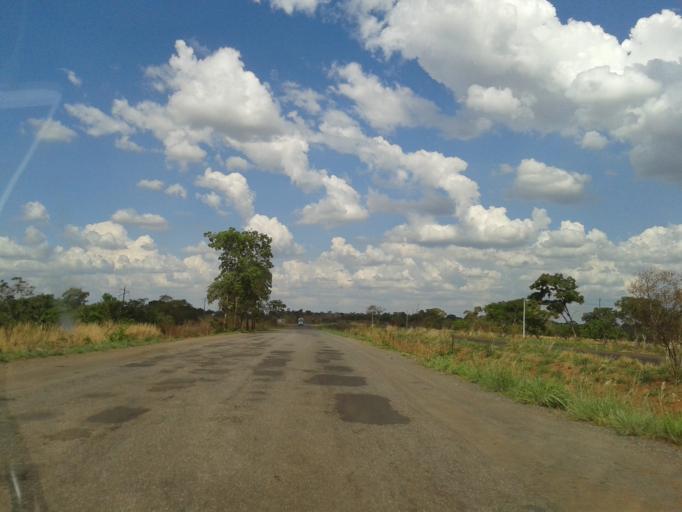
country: BR
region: Goias
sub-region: Caldas Novas
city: Caldas Novas
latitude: -17.6992
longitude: -48.7230
